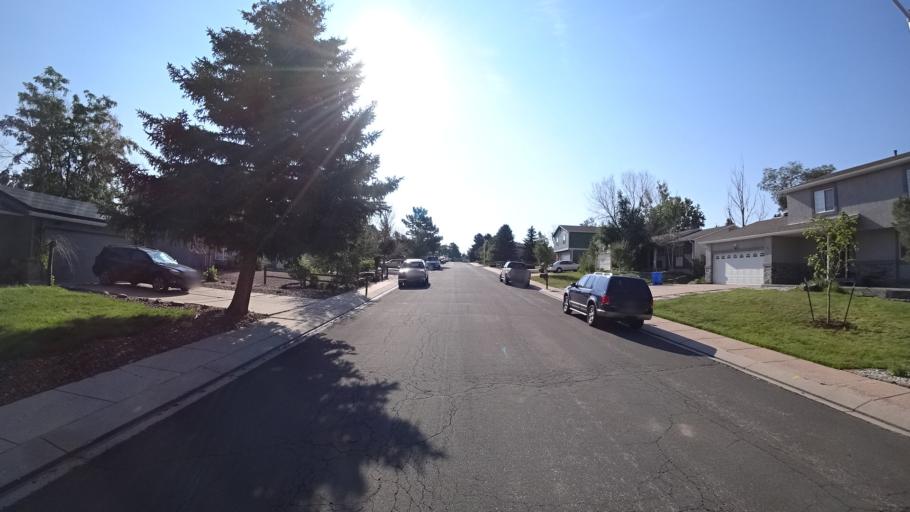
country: US
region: Colorado
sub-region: El Paso County
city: Air Force Academy
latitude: 38.9441
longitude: -104.7777
